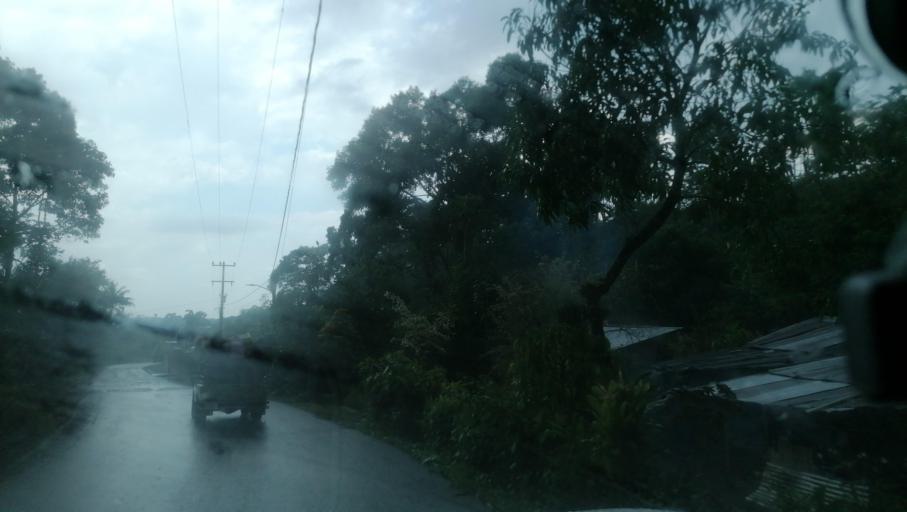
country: MX
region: Chiapas
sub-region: Cacahoatan
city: Benito Juarez
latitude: 15.0601
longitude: -92.1946
